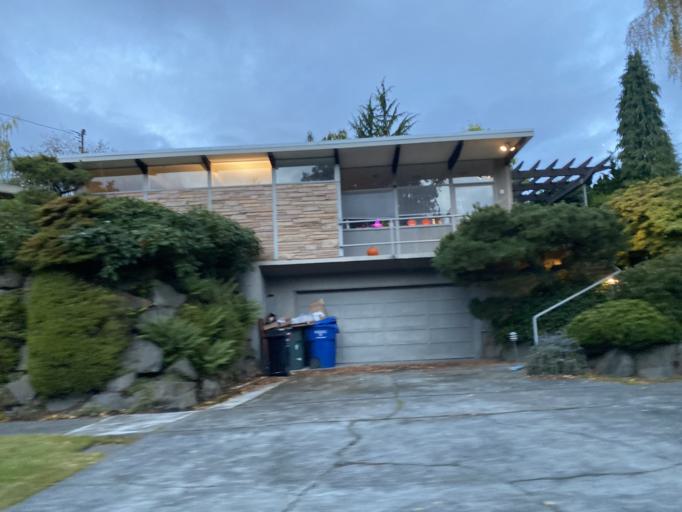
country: US
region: Washington
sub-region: King County
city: Seattle
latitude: 47.6527
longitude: -122.4090
